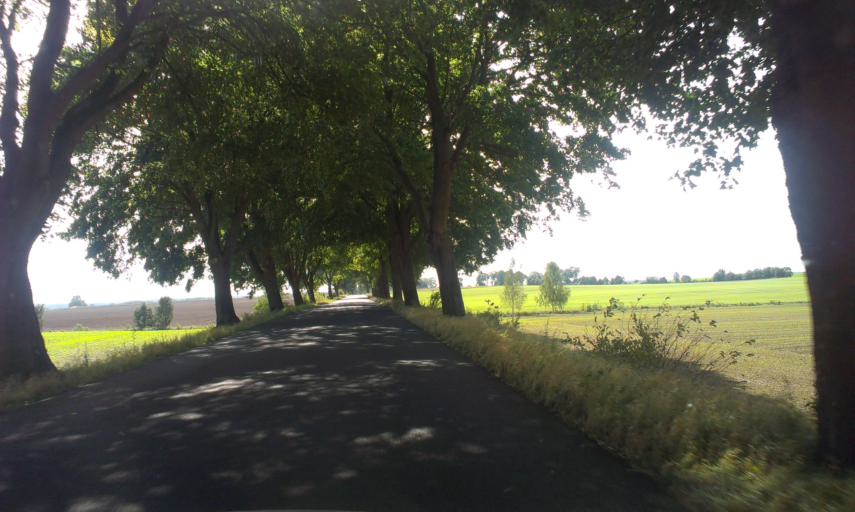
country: PL
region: Greater Poland Voivodeship
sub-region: Powiat zlotowski
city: Zlotow
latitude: 53.4630
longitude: 16.9877
